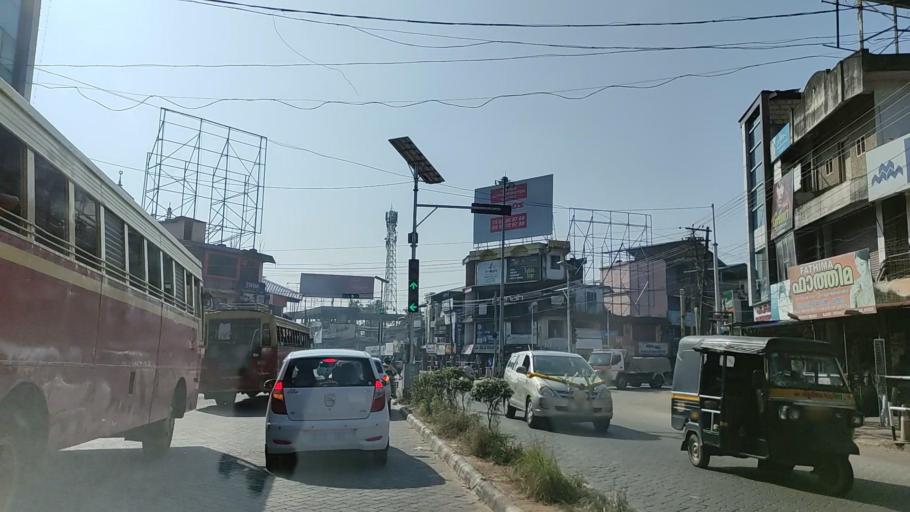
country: IN
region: Kerala
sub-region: Kollam
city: Punalur
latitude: 8.8980
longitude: 76.8603
